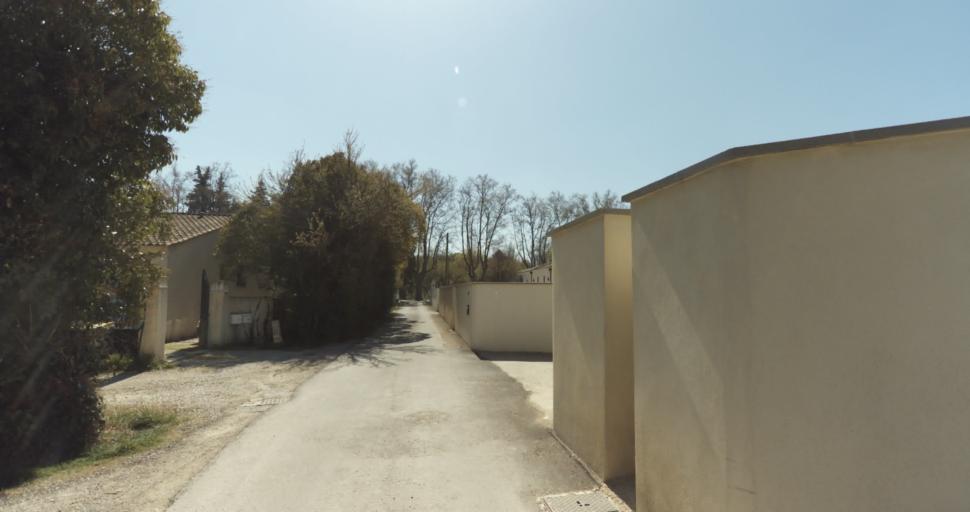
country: FR
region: Provence-Alpes-Cote d'Azur
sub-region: Departement des Bouches-du-Rhone
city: Pelissanne
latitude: 43.6302
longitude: 5.1699
